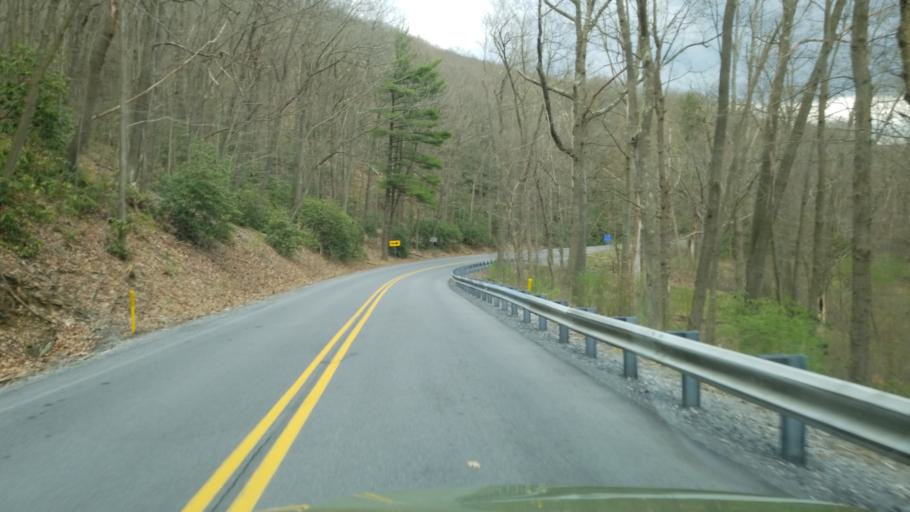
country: US
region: Pennsylvania
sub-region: Blair County
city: Tipton
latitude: 40.6742
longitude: -78.3258
